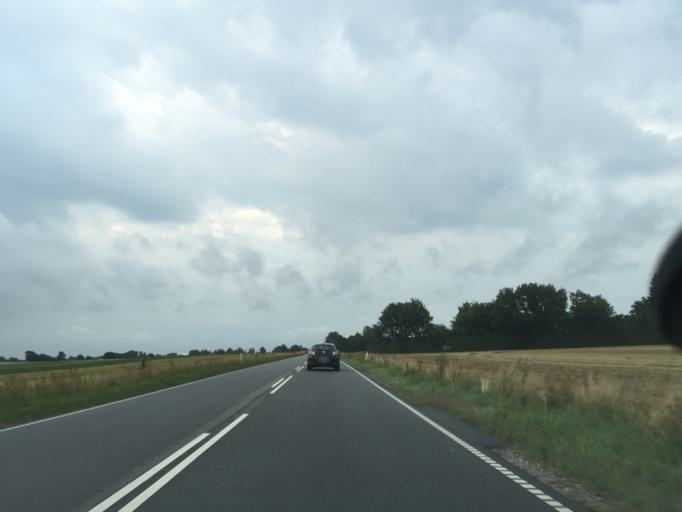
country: DK
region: Central Jutland
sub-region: Skanderborg Kommune
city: Galten
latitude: 56.1062
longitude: 9.8925
